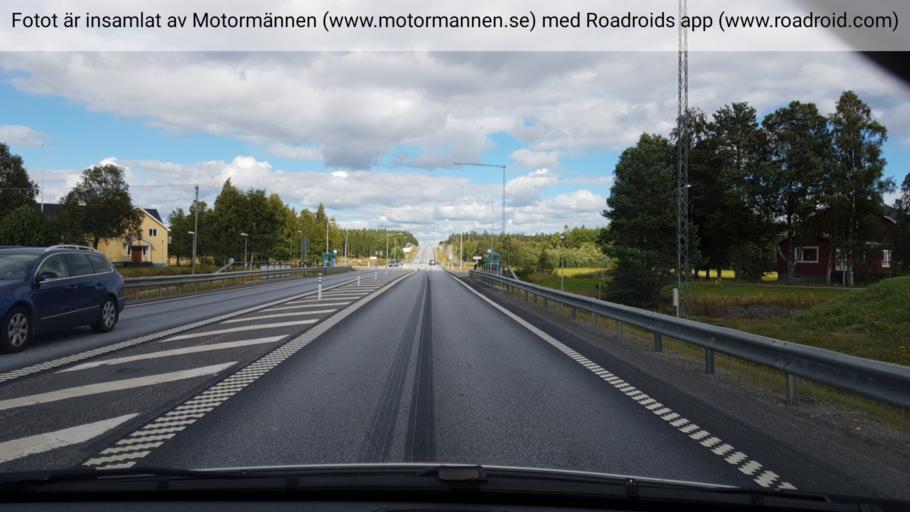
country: SE
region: Vaesterbotten
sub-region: Umea Kommun
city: Hoernefors
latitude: 63.6827
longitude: 20.0014
